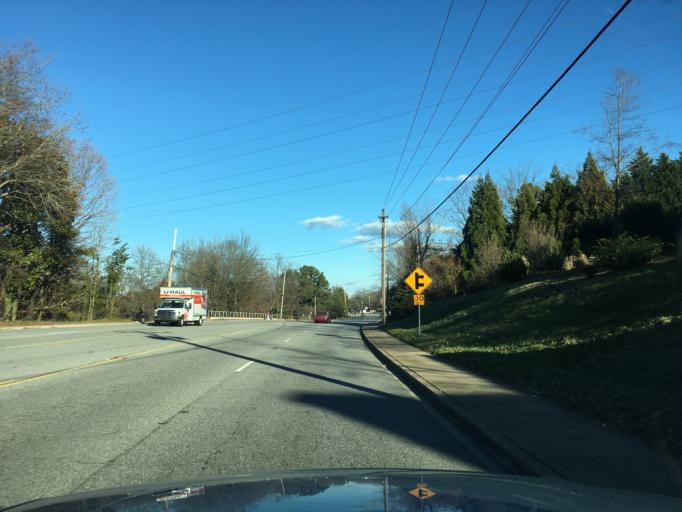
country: US
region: South Carolina
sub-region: Greenville County
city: Wade Hampton
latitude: 34.8702
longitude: -82.3484
